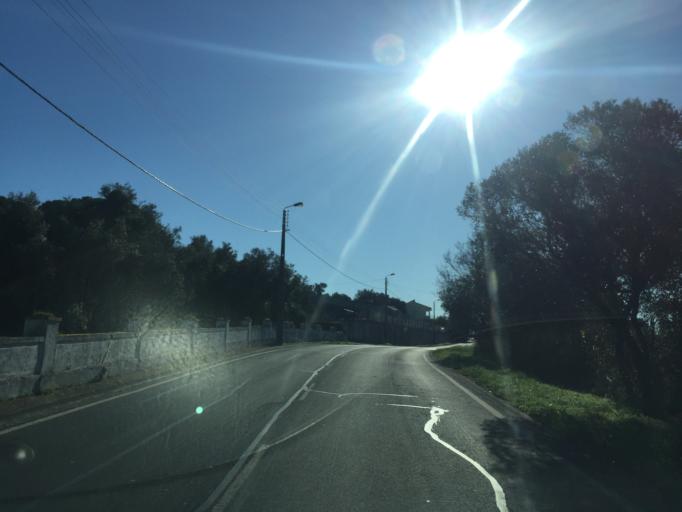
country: PT
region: Lisbon
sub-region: Sintra
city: Pero Pinheiro
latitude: 38.8366
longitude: -9.3102
